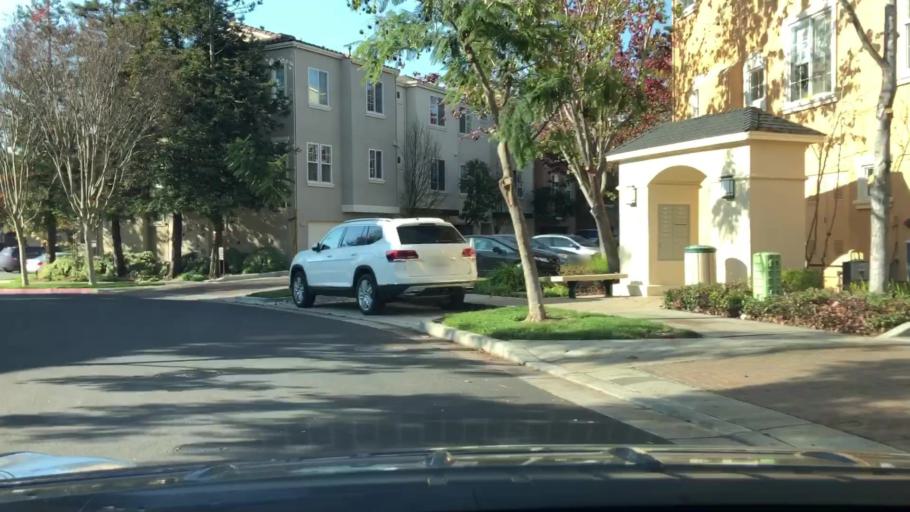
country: US
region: California
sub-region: Santa Clara County
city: Santa Clara
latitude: 37.4018
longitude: -121.9508
